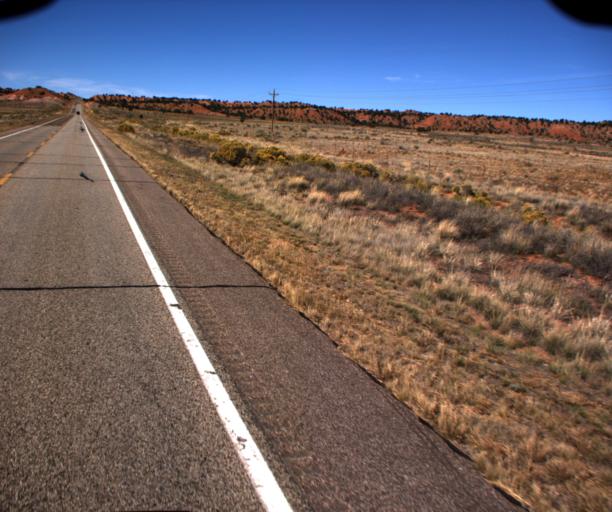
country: US
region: Arizona
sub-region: Mohave County
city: Colorado City
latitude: 36.8772
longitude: -112.8800
